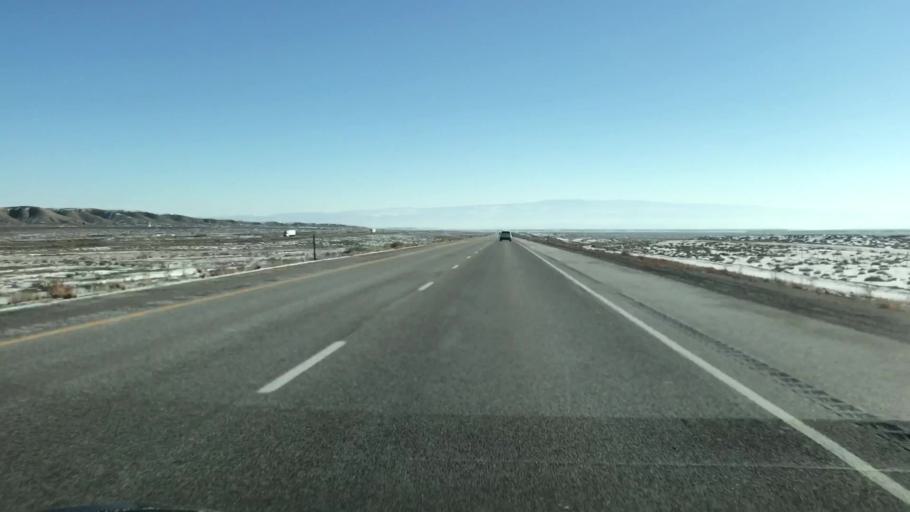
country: US
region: Utah
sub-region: Grand County
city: Moab
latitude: 38.9358
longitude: -109.4710
